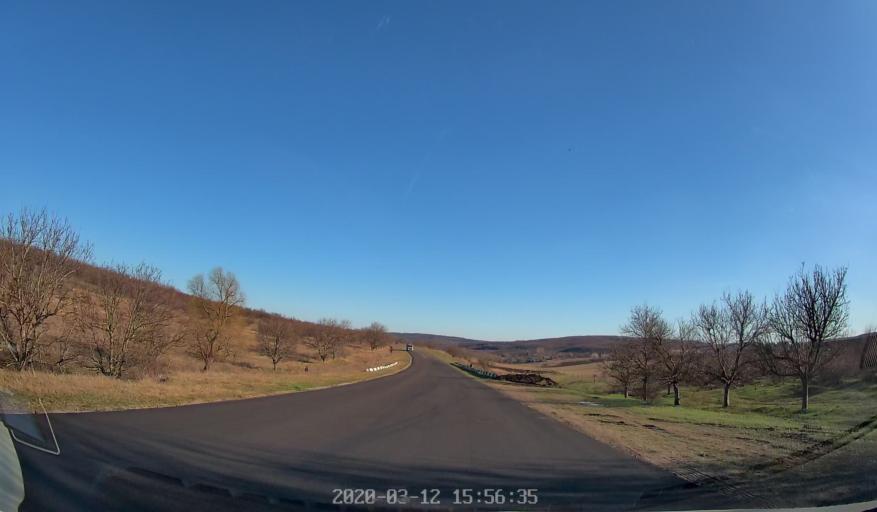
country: MD
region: Chisinau
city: Vadul lui Voda
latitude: 47.0619
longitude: 29.0339
